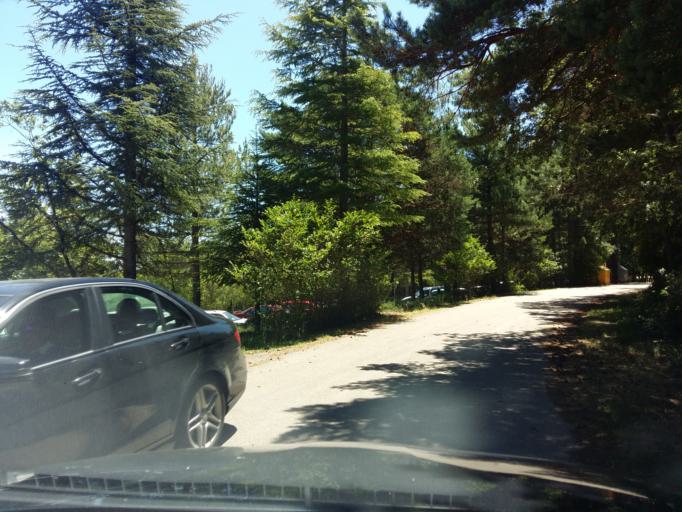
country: ES
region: Castille and Leon
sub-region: Provincia de Soria
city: Vozmediano
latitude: 41.8175
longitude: -1.8224
